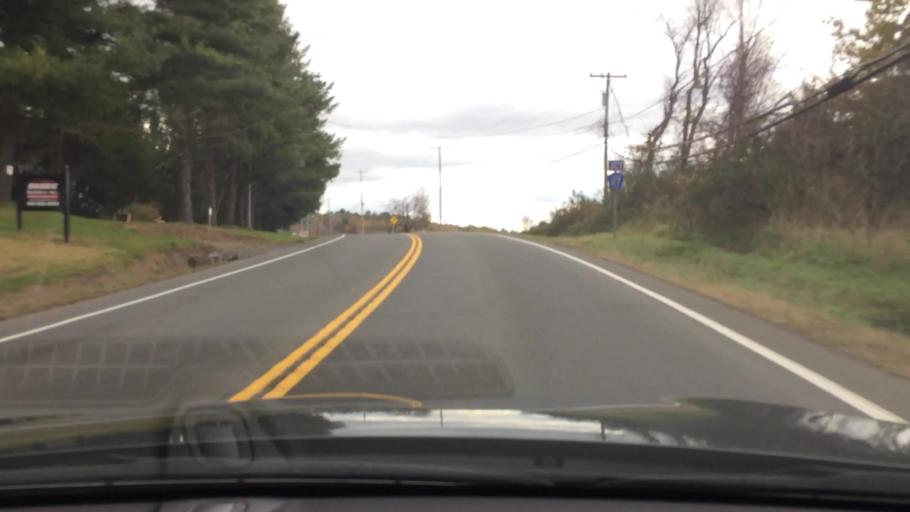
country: US
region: New York
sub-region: Columbia County
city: Oakdale
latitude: 42.2108
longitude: -73.7311
